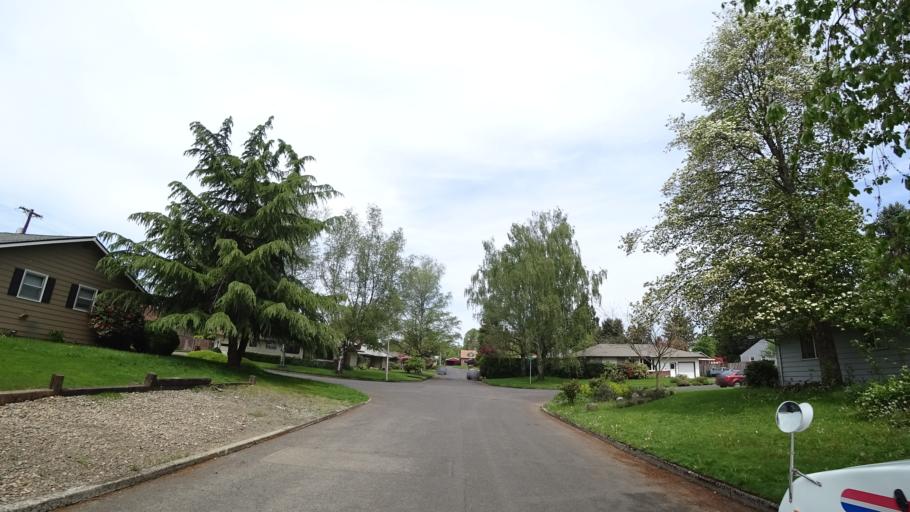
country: US
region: Oregon
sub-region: Clackamas County
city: Milwaukie
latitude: 45.4526
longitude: -122.6171
